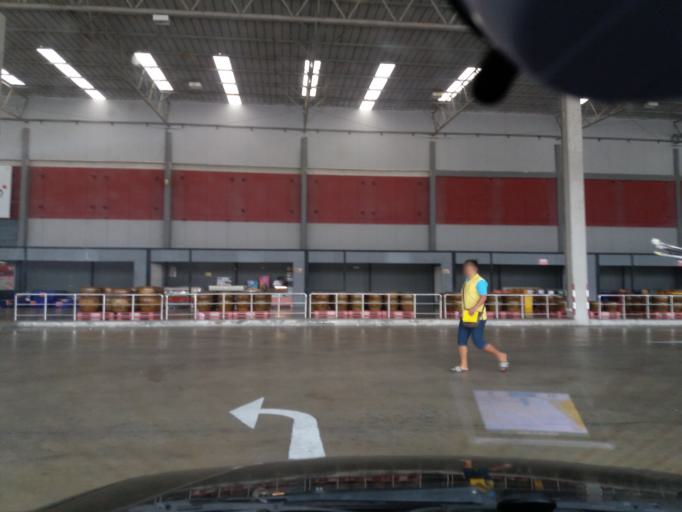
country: TH
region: Suphan Buri
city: Suphan Buri
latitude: 14.4766
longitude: 100.1328
